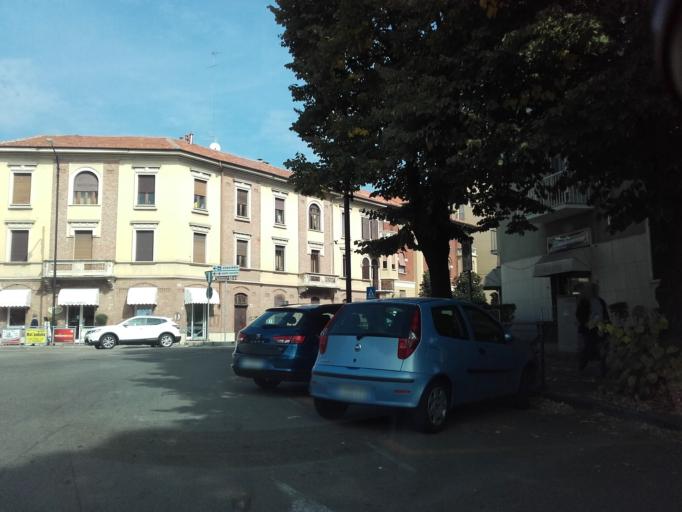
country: IT
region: Piedmont
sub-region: Provincia di Asti
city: Asti
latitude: 44.9038
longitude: 8.1995
